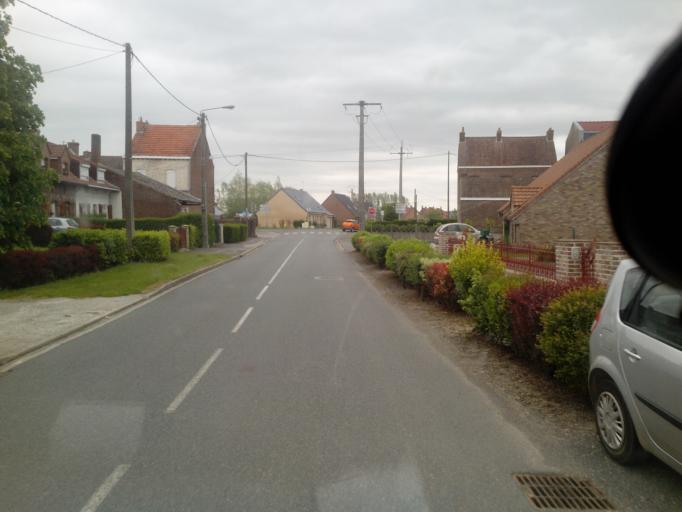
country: FR
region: Nord-Pas-de-Calais
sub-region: Departement du Nord
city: Vieux-Berquin
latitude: 50.6972
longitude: 2.6419
